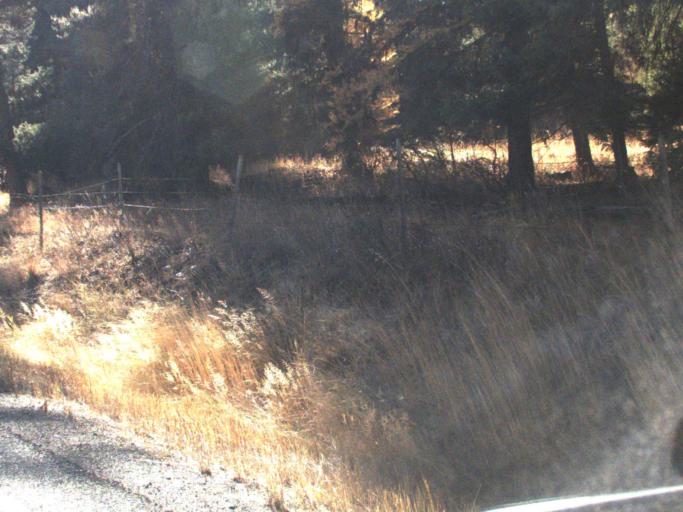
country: US
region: Washington
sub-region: Ferry County
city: Republic
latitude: 48.6101
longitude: -118.6614
